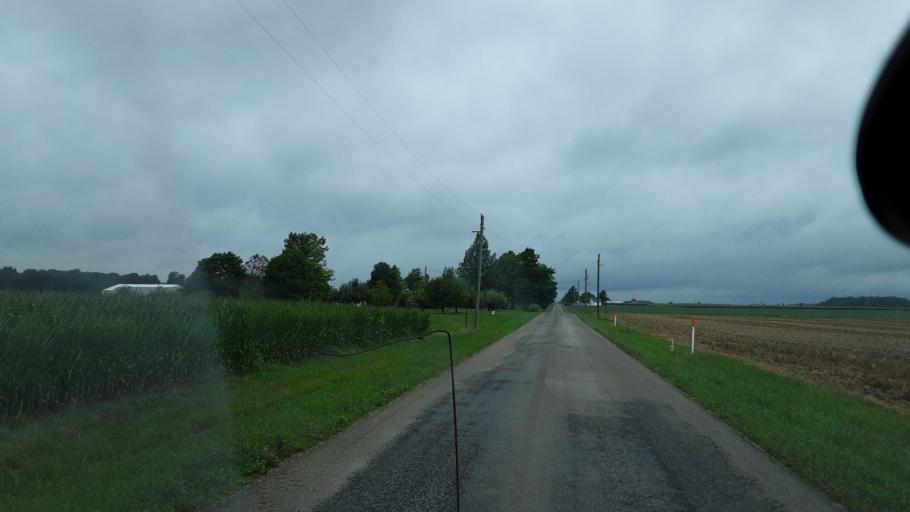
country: US
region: Indiana
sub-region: Allen County
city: Monroeville
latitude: 40.8939
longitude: -84.8425
